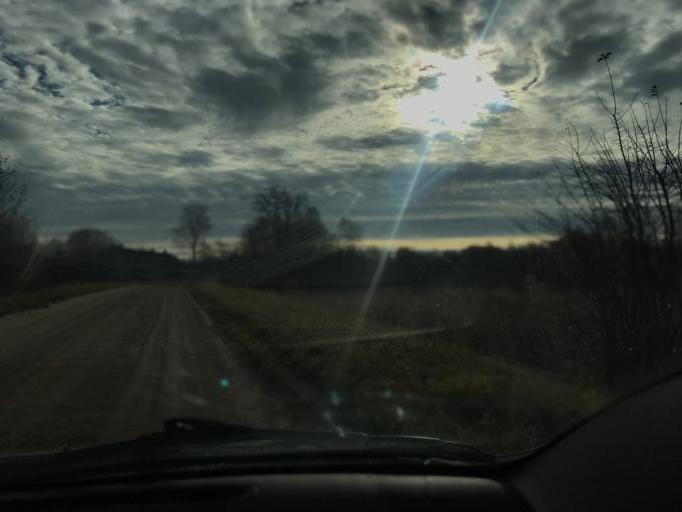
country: BY
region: Vitebsk
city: Haradok
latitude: 55.4537
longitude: 30.0343
